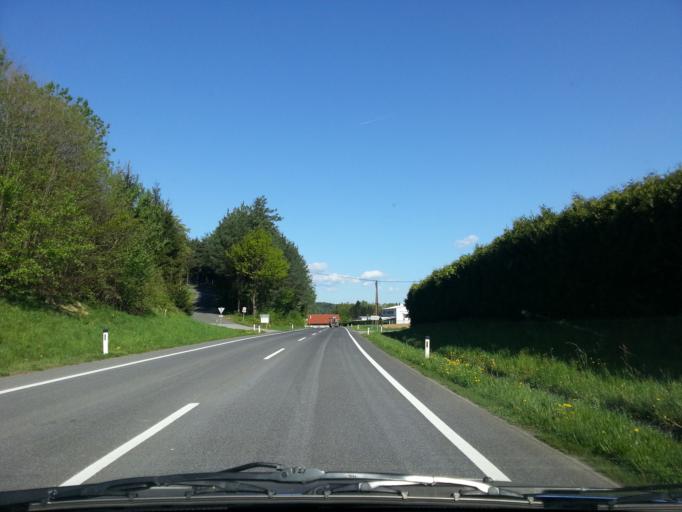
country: AT
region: Styria
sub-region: Politischer Bezirk Leibnitz
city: Arnfels
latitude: 46.6834
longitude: 15.3850
